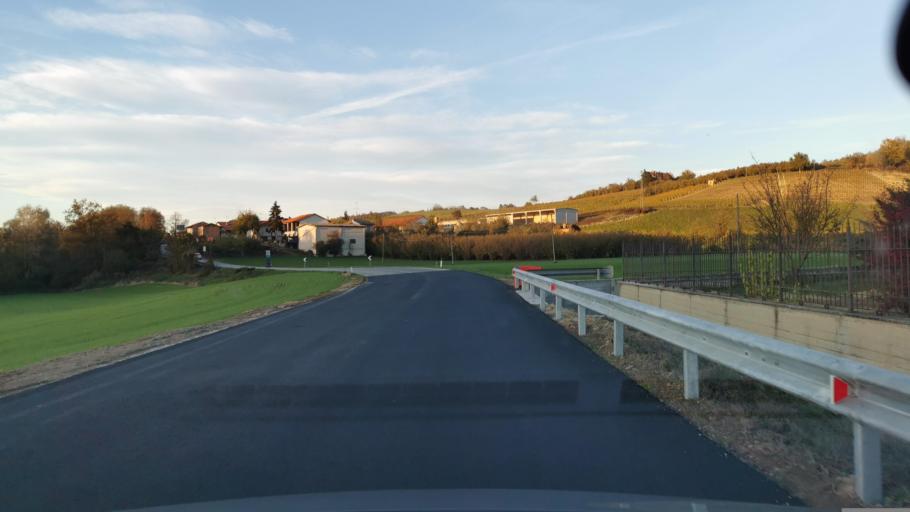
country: IT
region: Piedmont
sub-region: Provincia di Cuneo
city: Narzole
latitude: 44.5931
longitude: 7.8941
